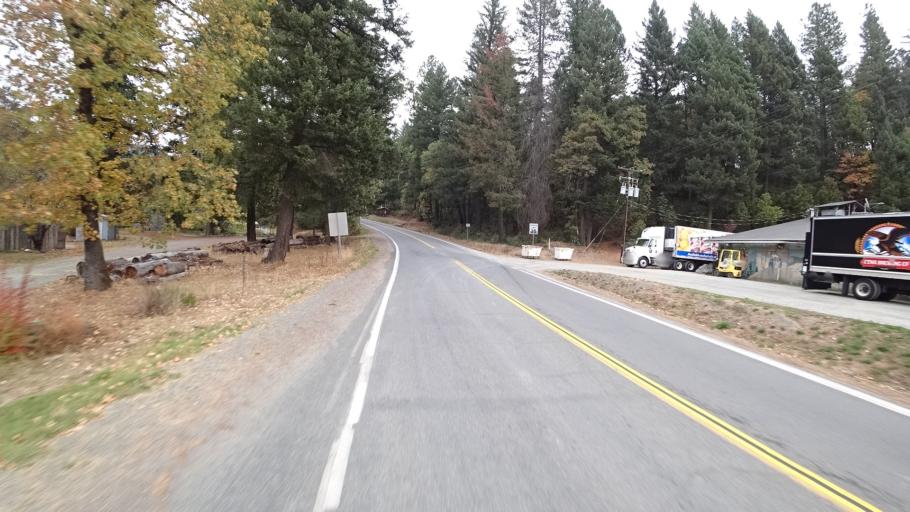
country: US
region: California
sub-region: Siskiyou County
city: Happy Camp
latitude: 41.7999
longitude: -123.3773
